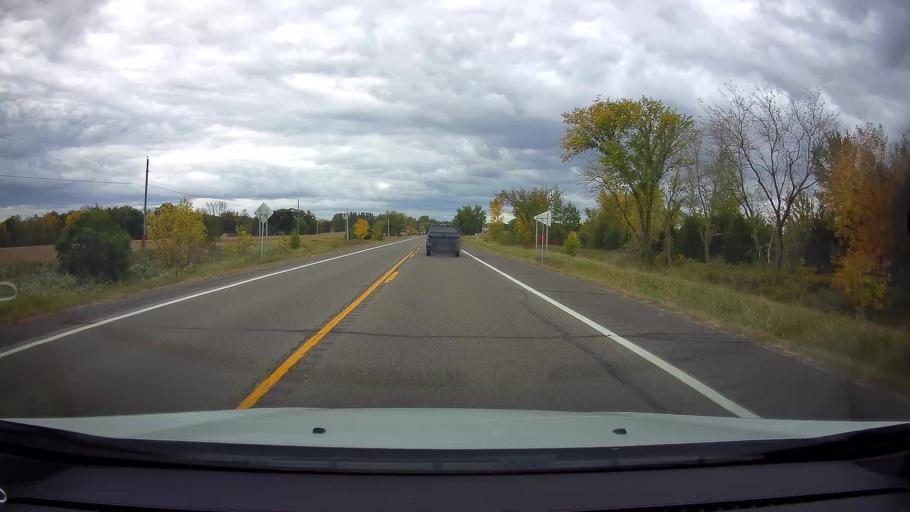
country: US
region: Minnesota
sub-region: Chisago County
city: Chisago City
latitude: 45.3510
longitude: -92.9117
